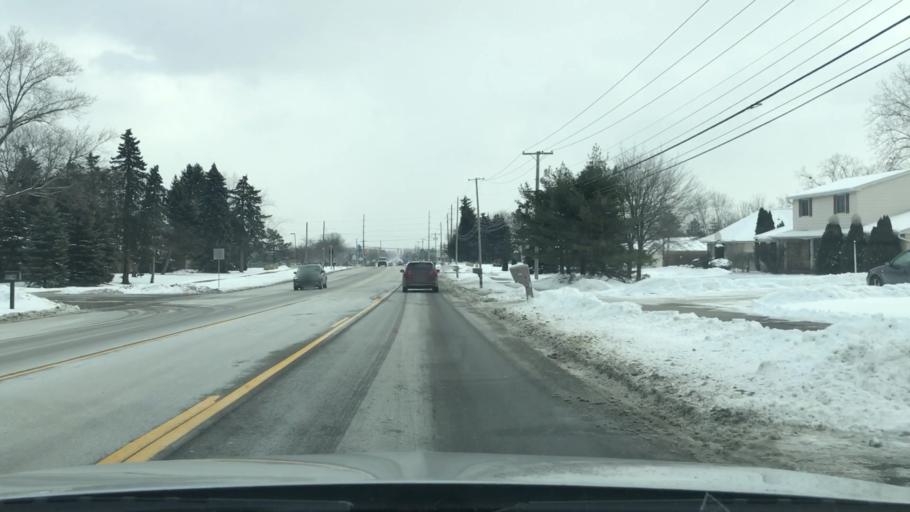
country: US
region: Michigan
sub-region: Oakland County
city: Rochester Hills
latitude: 42.6523
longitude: -83.1366
